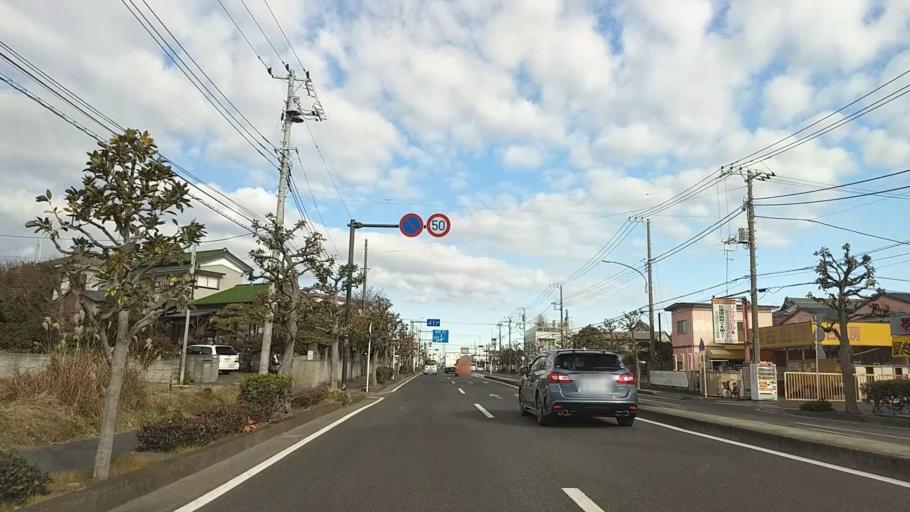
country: JP
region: Kanagawa
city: Hiratsuka
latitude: 35.3466
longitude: 139.3563
